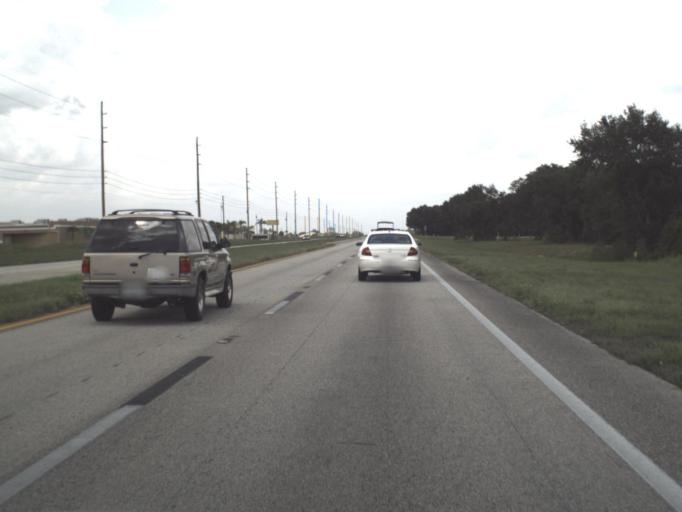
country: US
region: Florida
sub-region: Polk County
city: Lake Wales
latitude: 27.8691
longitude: -81.5925
